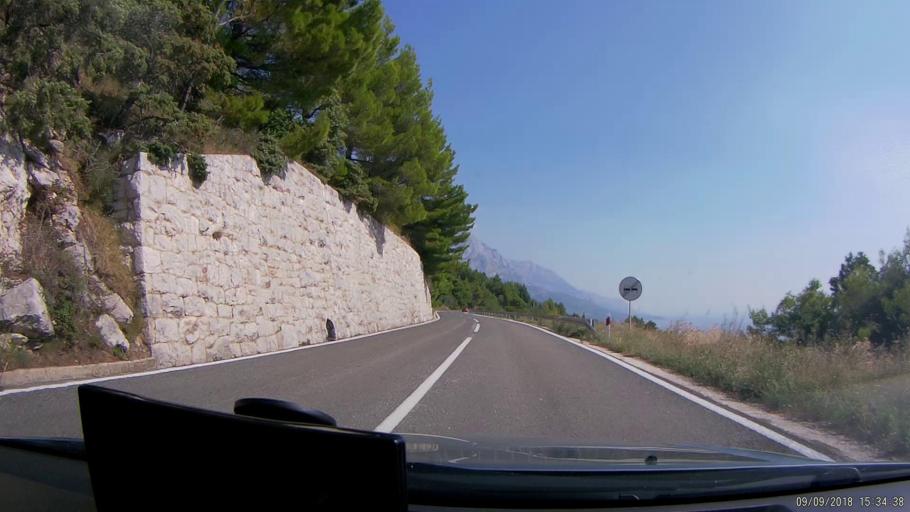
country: HR
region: Splitsko-Dalmatinska
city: Donja Brela
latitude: 43.3875
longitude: 16.9067
